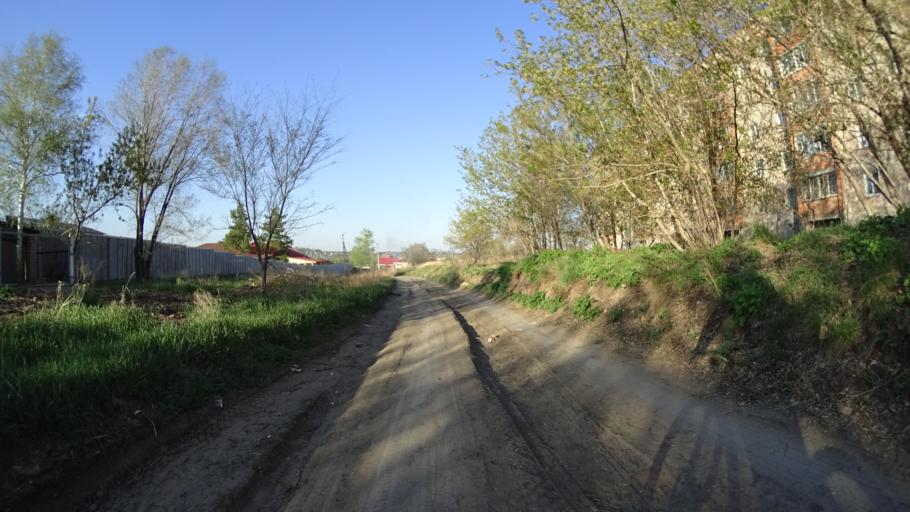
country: RU
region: Chelyabinsk
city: Troitsk
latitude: 54.0866
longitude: 61.5349
